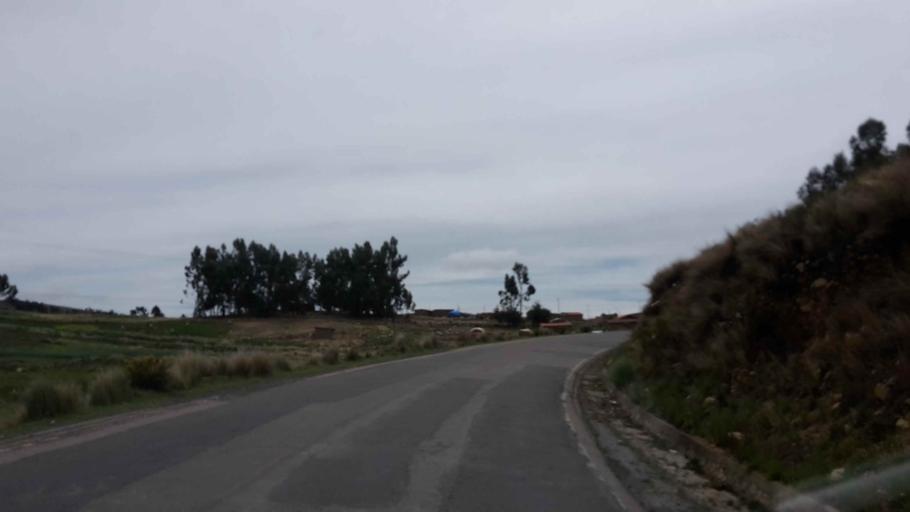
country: BO
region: Cochabamba
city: Arani
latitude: -17.4862
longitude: -65.6077
